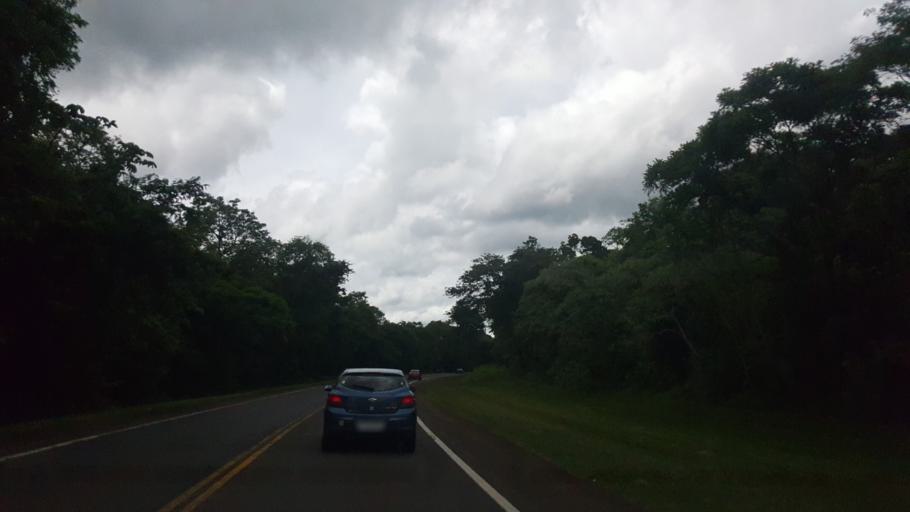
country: AR
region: Misiones
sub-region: Departamento de Iguazu
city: Puerto Iguazu
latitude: -25.6915
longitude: -54.5147
